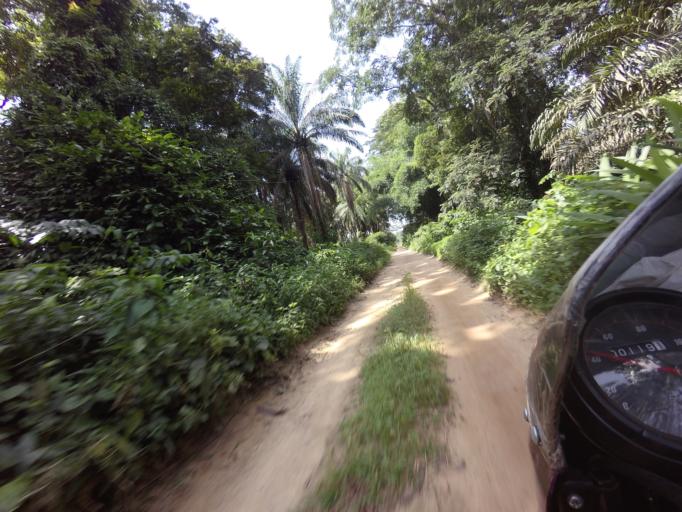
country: SL
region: Eastern Province
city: Manowa
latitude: 8.1519
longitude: -10.7582
